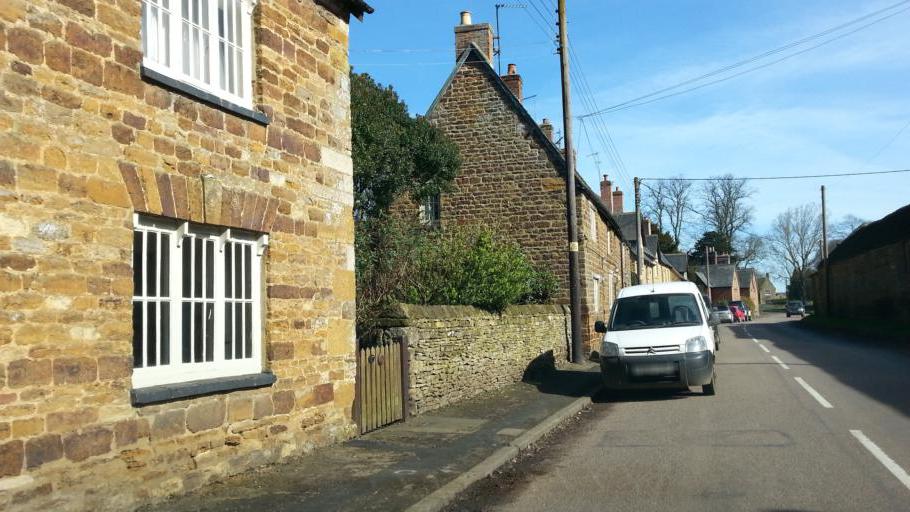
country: GB
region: England
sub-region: Northamptonshire
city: Brixworth
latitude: 52.3643
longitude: -0.8866
